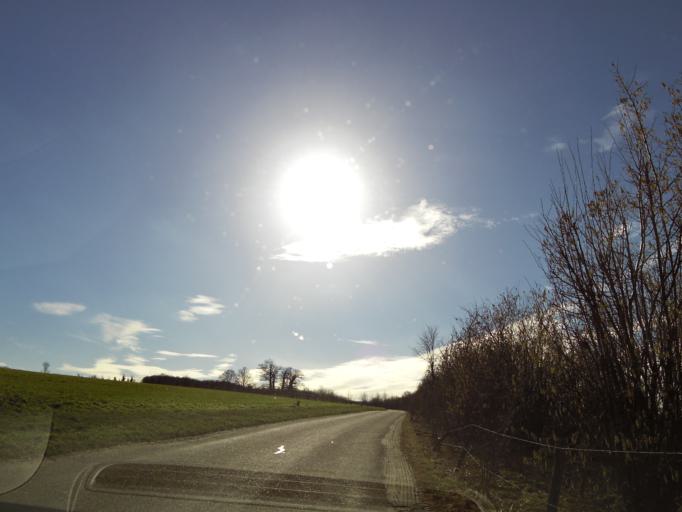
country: NL
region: Limburg
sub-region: Valkenburg aan de Geul
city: Schin op Geul
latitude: 50.8056
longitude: 5.8858
